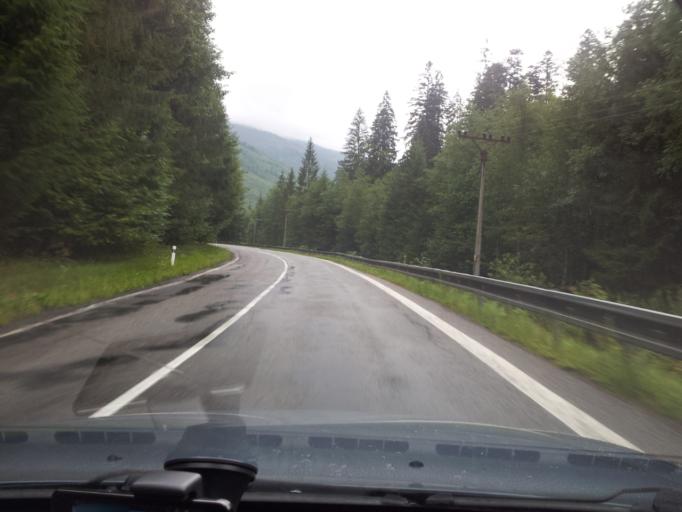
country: SK
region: Banskobystricky
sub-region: Okres Banska Bystrica
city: Brezno
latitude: 48.8705
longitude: 19.6528
